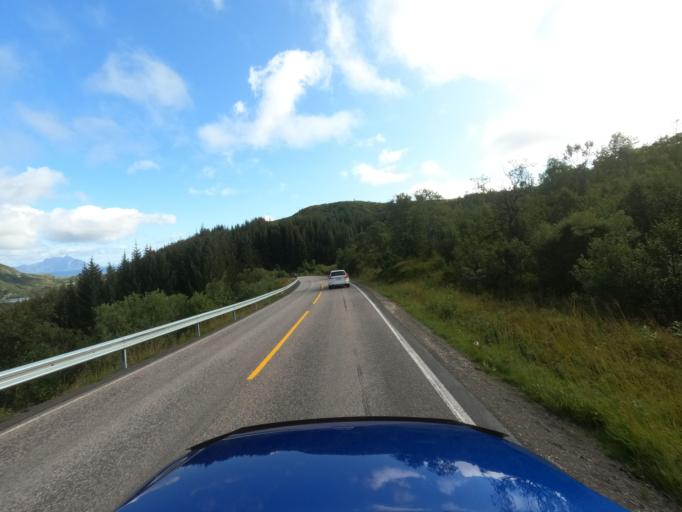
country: NO
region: Nordland
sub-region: Vestvagoy
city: Leknes
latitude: 68.1561
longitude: 13.7077
